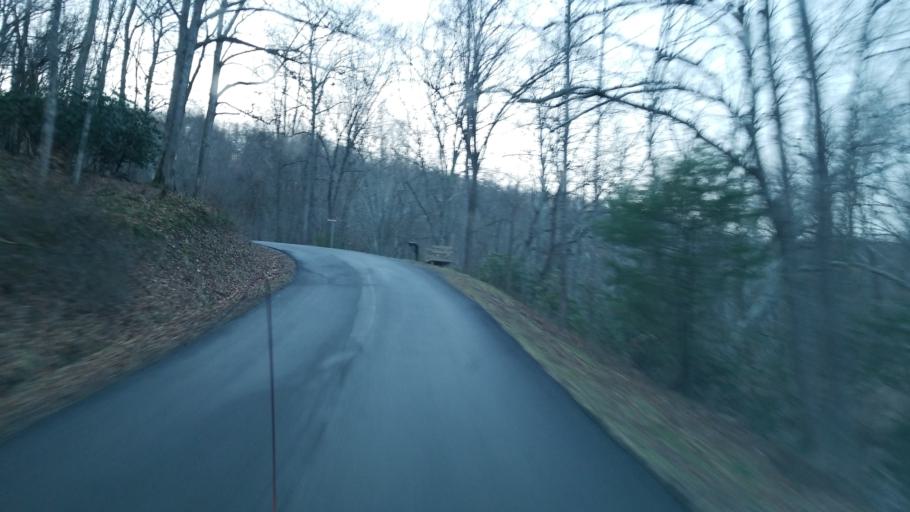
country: US
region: Virginia
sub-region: Pulaski County
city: Pulaski
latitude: 37.1521
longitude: -80.8707
